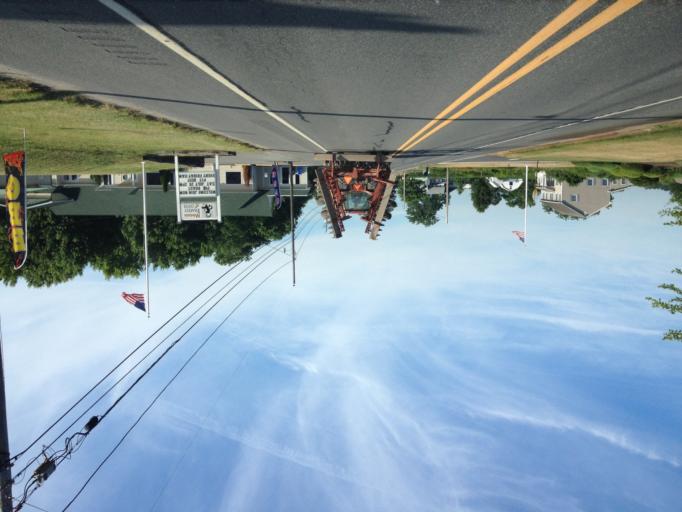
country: US
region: Delaware
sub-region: Sussex County
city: Selbyville
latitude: 38.4872
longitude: -75.1604
